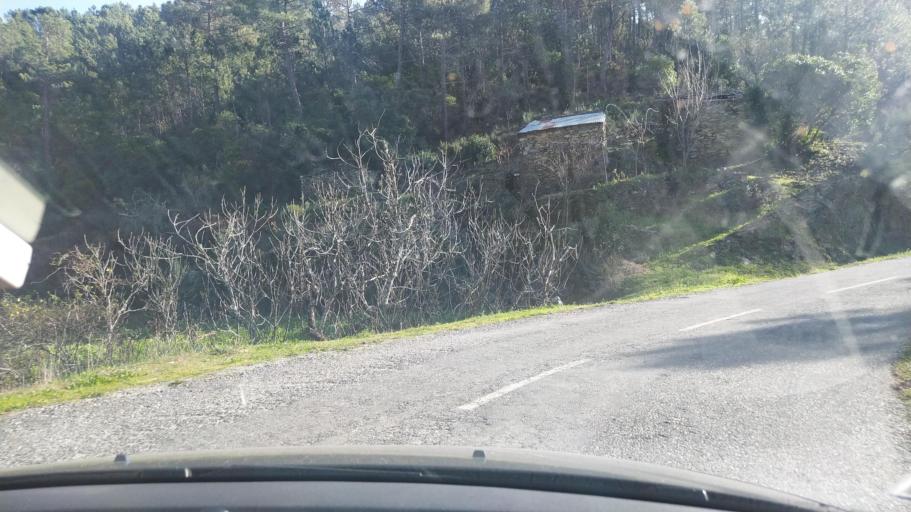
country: PT
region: Coimbra
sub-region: Oliveira do Hospital
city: Oliveira do Hospital
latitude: 40.2063
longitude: -7.7303
